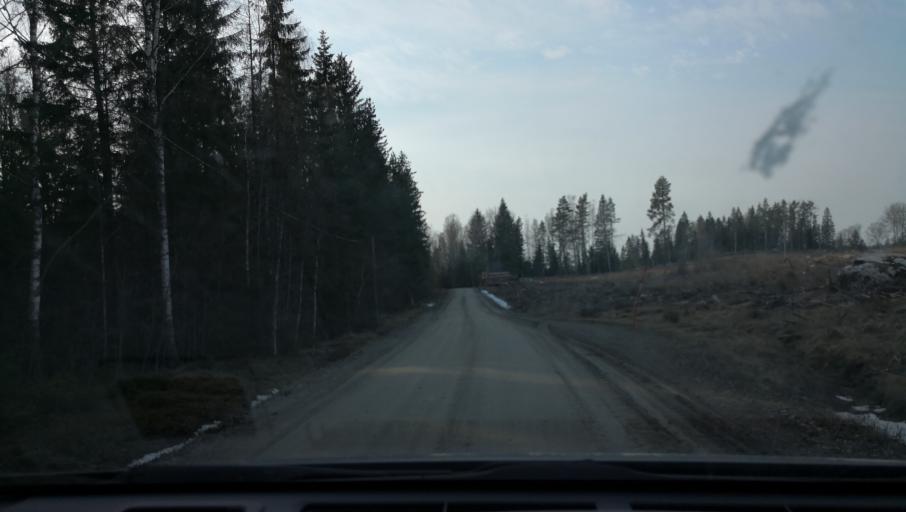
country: SE
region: OErebro
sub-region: Orebro Kommun
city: Hovsta
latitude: 59.3821
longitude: 15.2817
